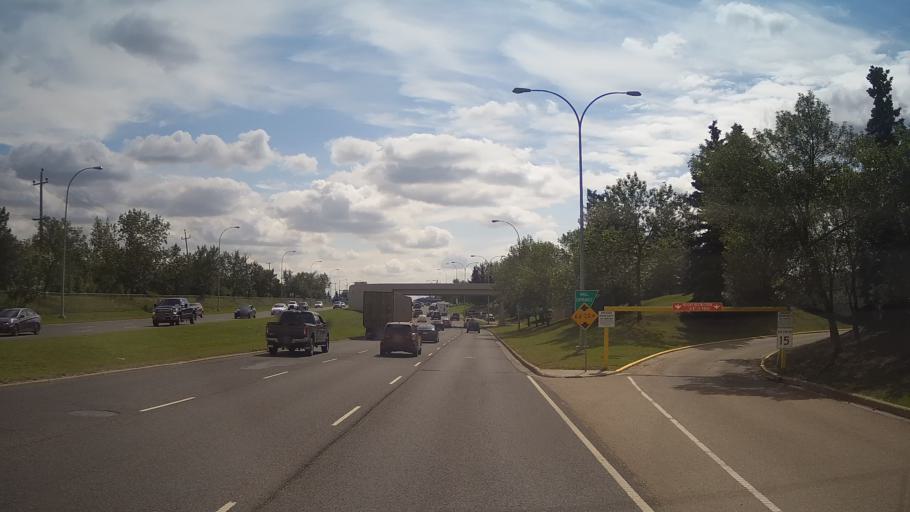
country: CA
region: Alberta
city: St. Albert
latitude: 53.5228
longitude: -113.6155
